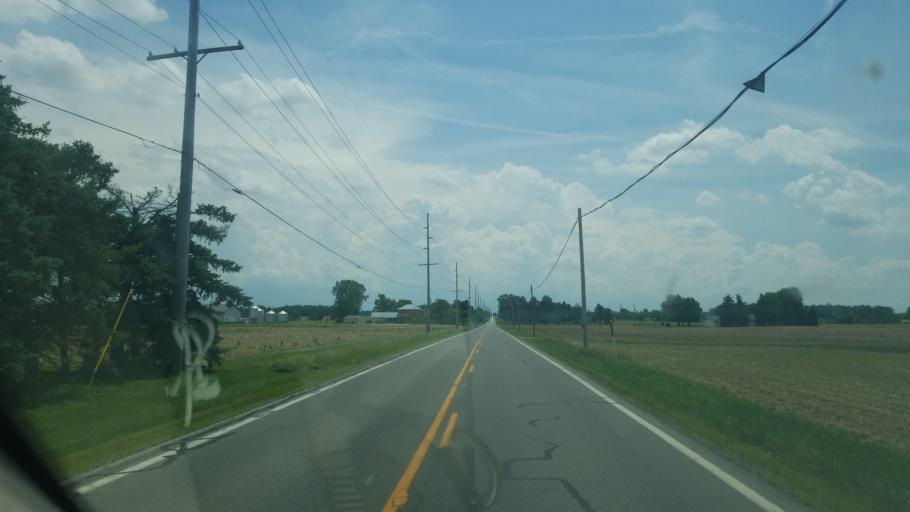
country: US
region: Ohio
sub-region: Hancock County
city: Arlington
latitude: 40.7826
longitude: -83.6519
